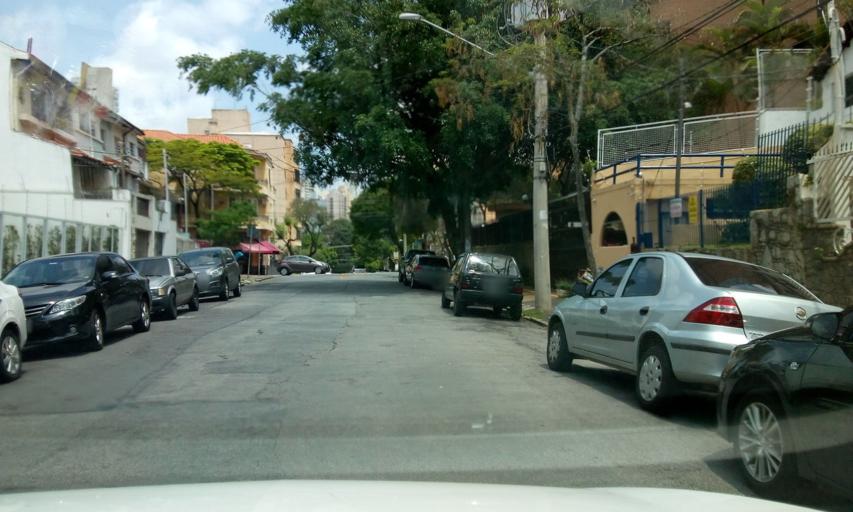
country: BR
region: Sao Paulo
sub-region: Sao Paulo
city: Sao Paulo
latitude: -23.5719
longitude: -46.6316
